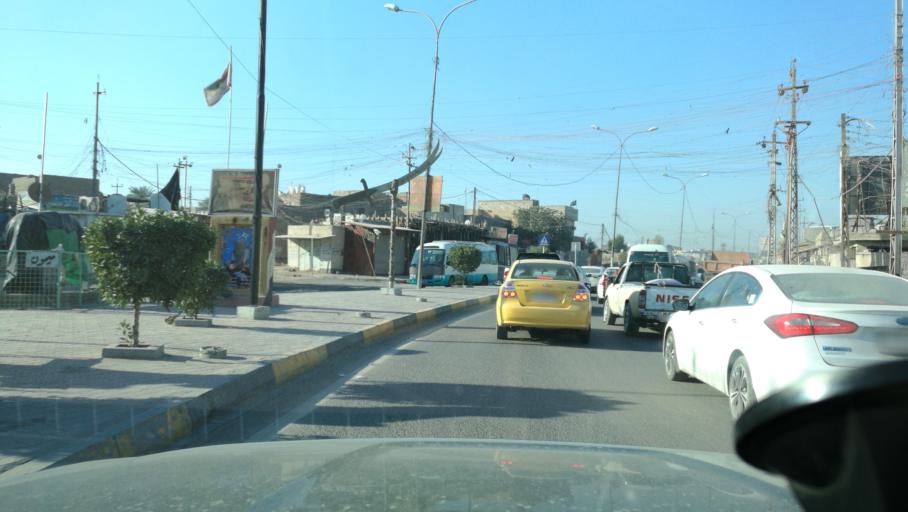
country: IQ
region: Basra Governorate
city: Al Basrah al Qadimah
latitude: 30.4937
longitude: 47.8185
